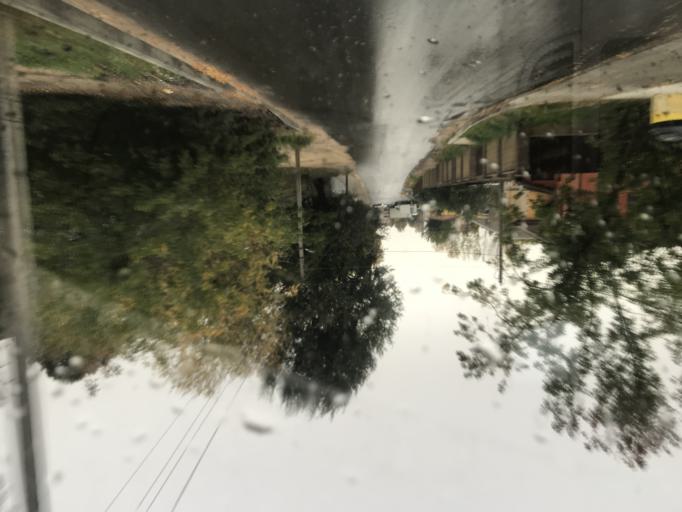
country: BY
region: Mogilev
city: Mahilyow
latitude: 53.8968
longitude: 30.3220
